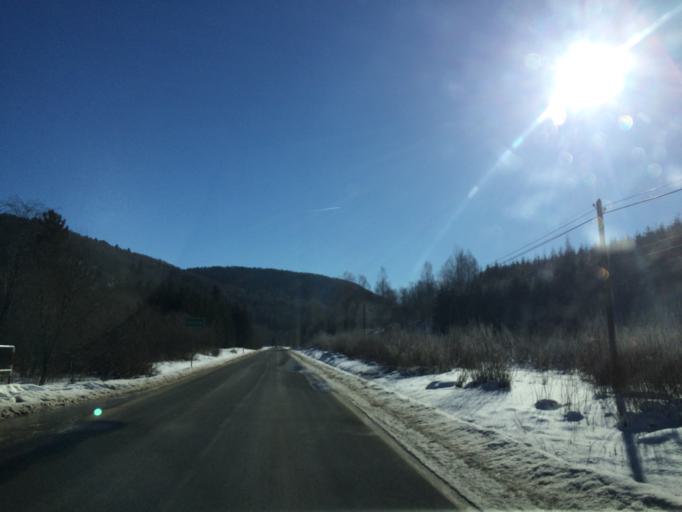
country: PL
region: Subcarpathian Voivodeship
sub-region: Powiat bieszczadzki
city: Lutowiska
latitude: 49.1977
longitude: 22.6772
